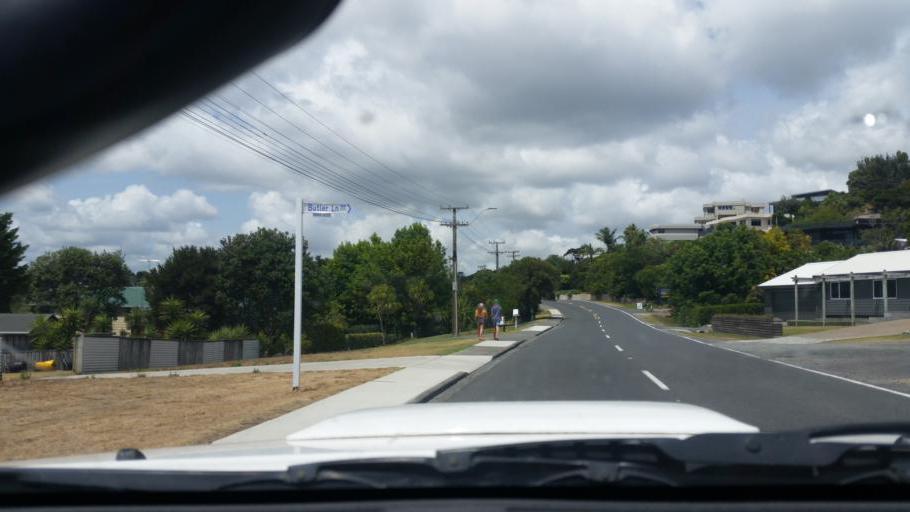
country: NZ
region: Auckland
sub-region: Auckland
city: Wellsford
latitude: -36.0919
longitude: 174.5846
